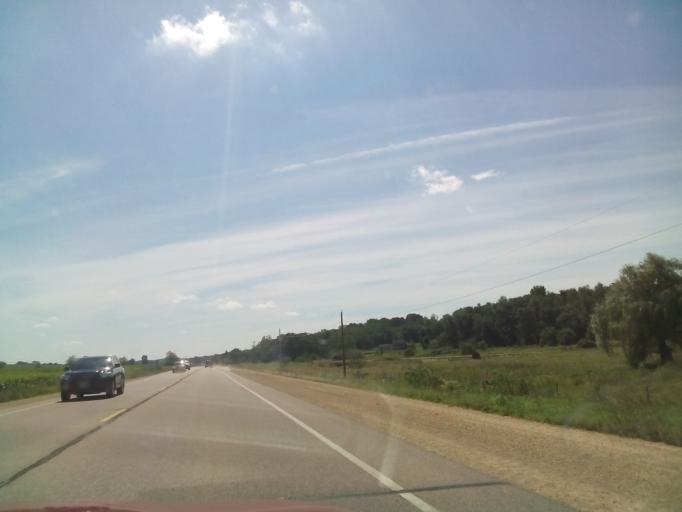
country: US
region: Wisconsin
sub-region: Green County
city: Monticello
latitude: 42.7652
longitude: -89.6208
